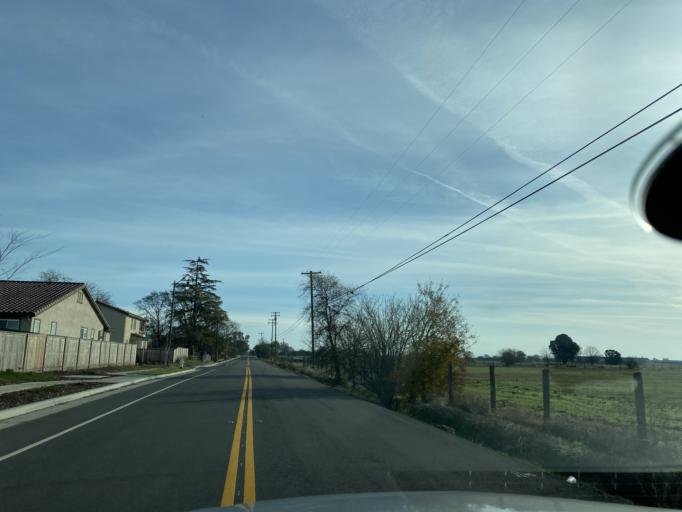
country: US
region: California
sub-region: Sacramento County
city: Elk Grove
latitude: 38.3908
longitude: -121.3964
